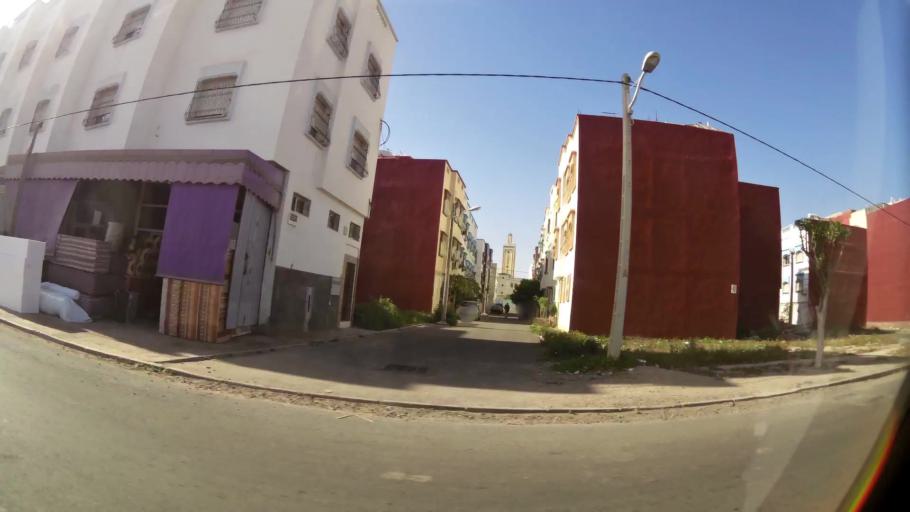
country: MA
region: Souss-Massa-Draa
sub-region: Inezgane-Ait Mellou
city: Inezgane
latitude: 30.3734
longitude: -9.5144
